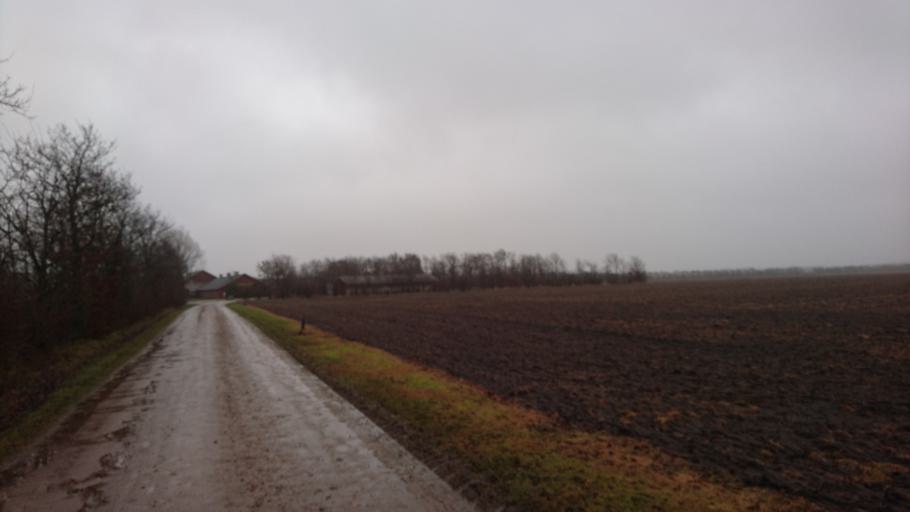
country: DK
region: Central Jutland
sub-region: Herning Kommune
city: Sunds
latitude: 56.1925
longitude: 9.0280
